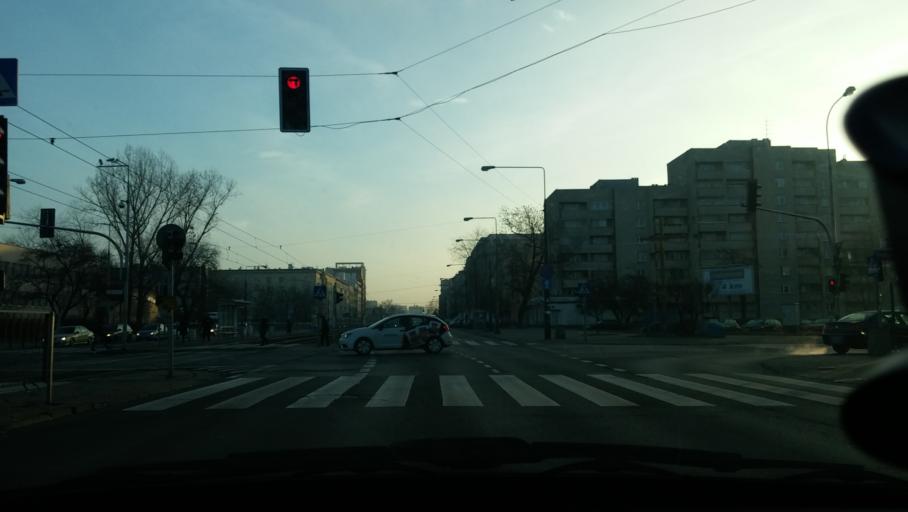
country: PL
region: Masovian Voivodeship
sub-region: Warszawa
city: Praga Poludnie
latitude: 52.2458
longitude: 21.0744
